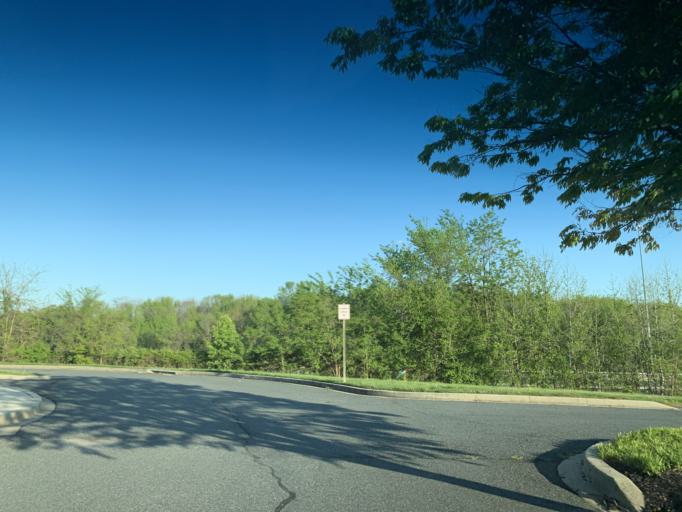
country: US
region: Maryland
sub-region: Harford County
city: Aberdeen
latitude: 39.5298
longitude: -76.1860
